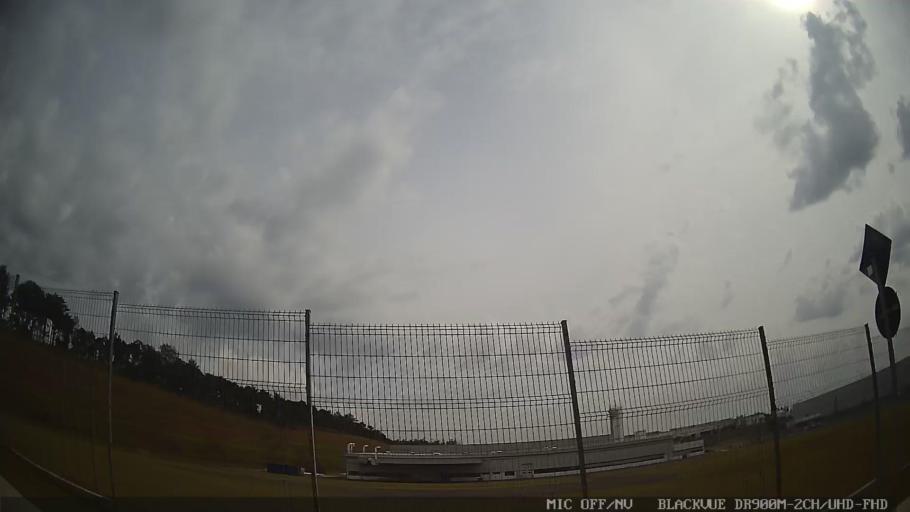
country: BR
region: Sao Paulo
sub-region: Indaiatuba
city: Indaiatuba
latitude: -23.1139
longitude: -47.2780
